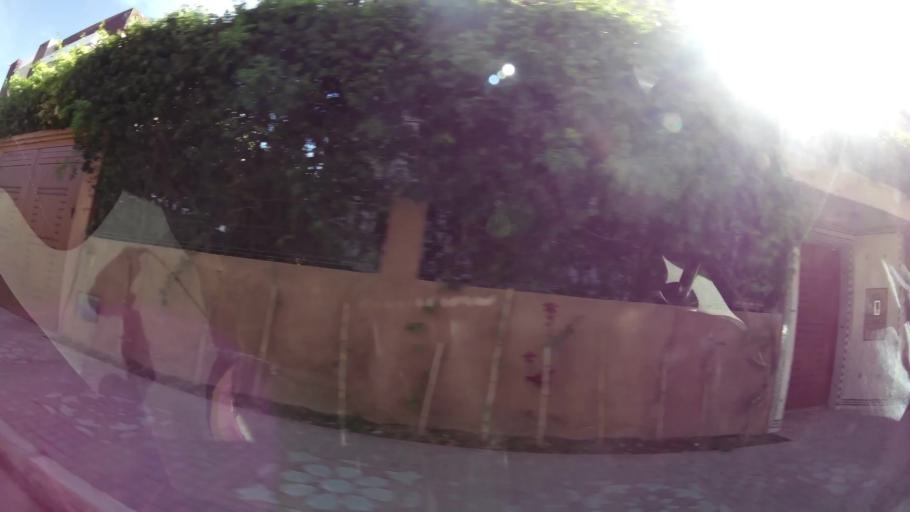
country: MA
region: Marrakech-Tensift-Al Haouz
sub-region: Marrakech
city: Marrakesh
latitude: 31.6476
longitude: -8.0443
